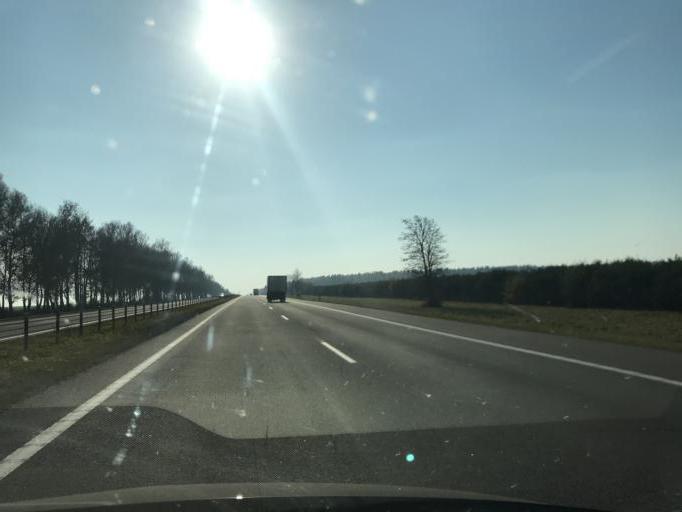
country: BY
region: Minsk
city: Enyerhyetykaw
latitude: 53.6472
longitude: 27.0712
